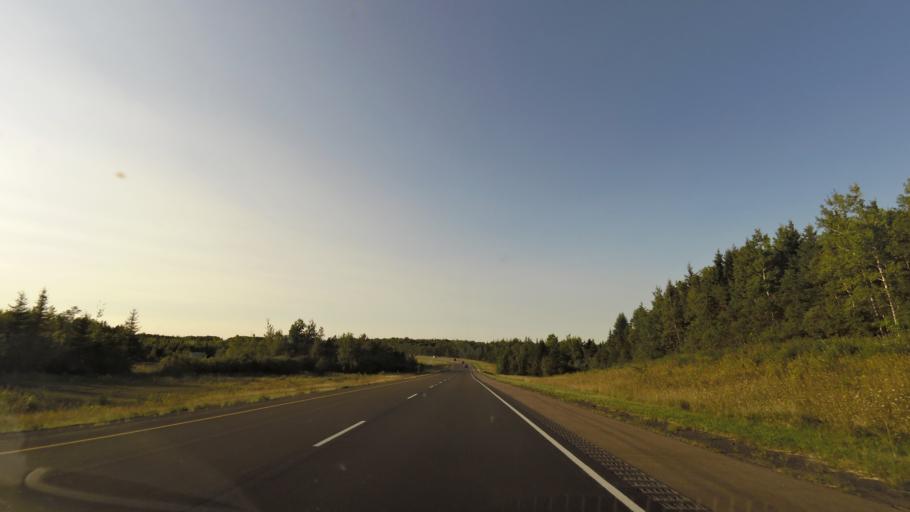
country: CA
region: New Brunswick
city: Dieppe
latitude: 46.0894
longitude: -64.5960
